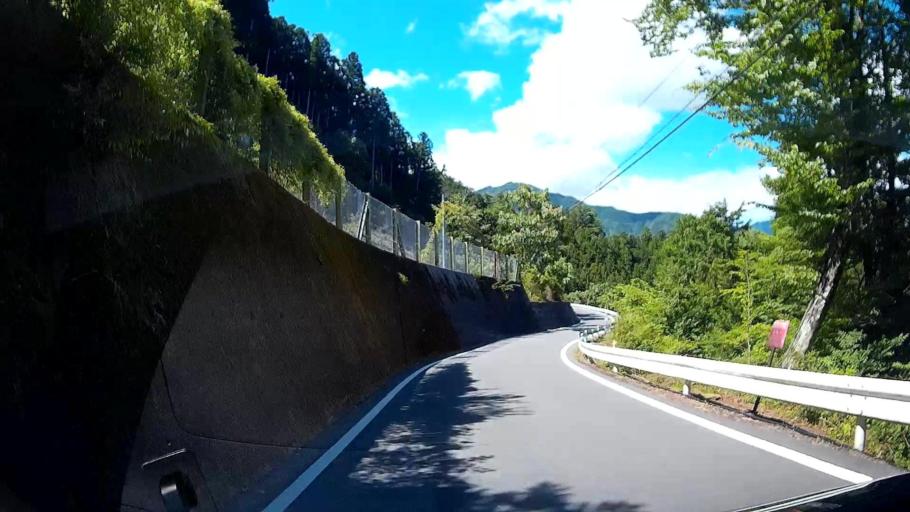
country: JP
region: Shizuoka
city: Shizuoka-shi
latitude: 35.2011
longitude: 138.2369
